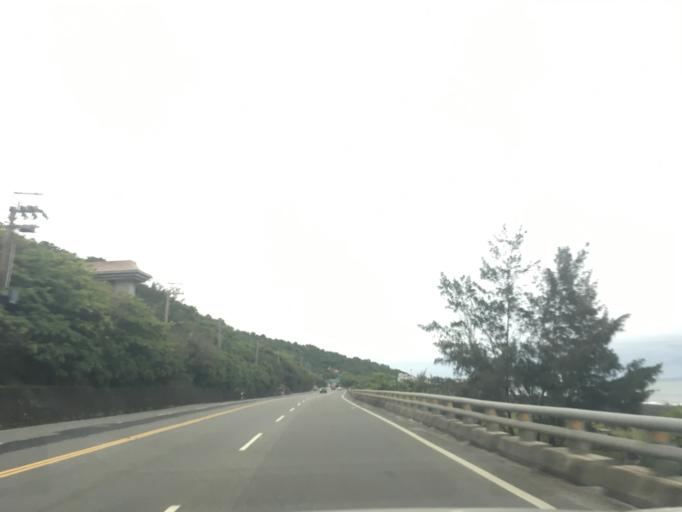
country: TW
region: Taiwan
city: Hengchun
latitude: 22.3494
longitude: 120.9006
